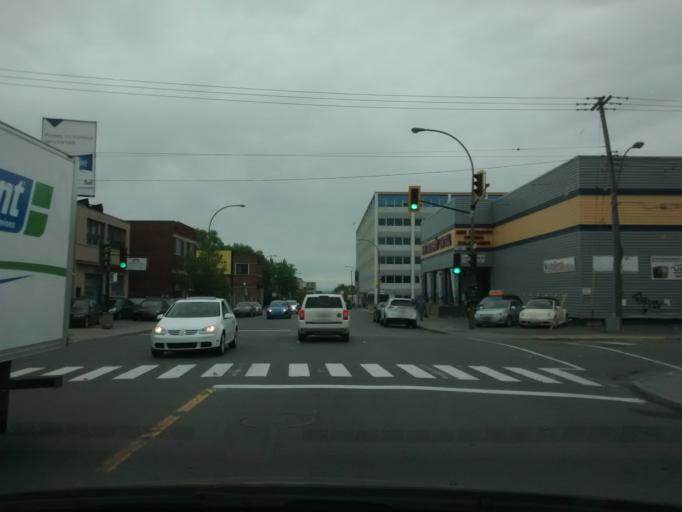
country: CA
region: Quebec
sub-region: Montreal
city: Montreal
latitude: 45.5453
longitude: -73.5836
